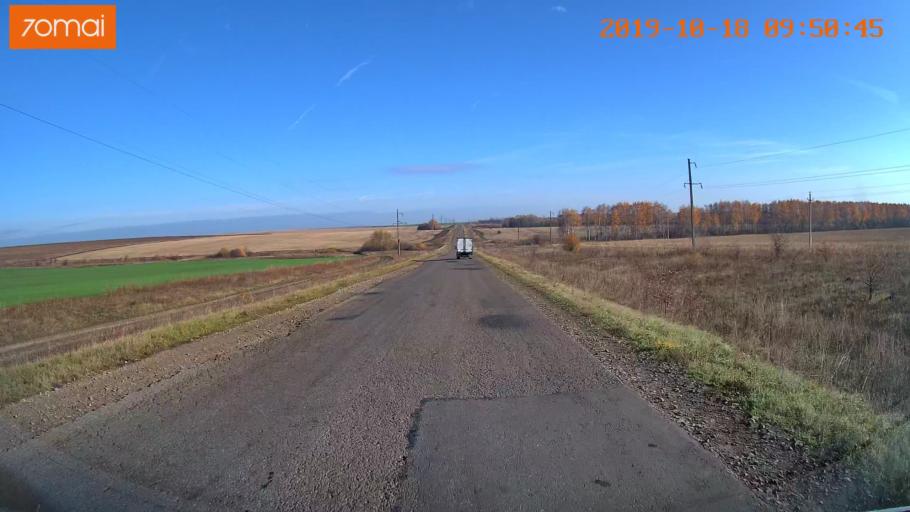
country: RU
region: Tula
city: Kazachka
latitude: 53.3323
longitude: 38.2818
